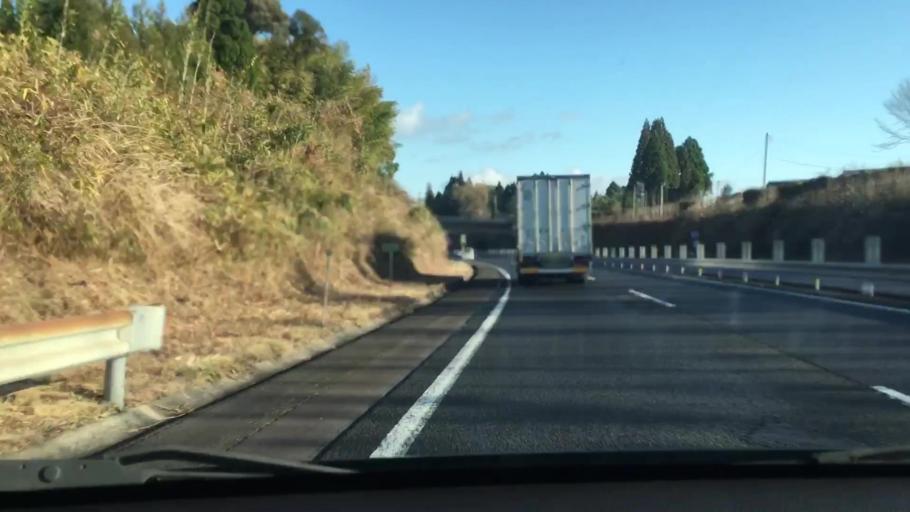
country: JP
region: Kagoshima
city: Kajiki
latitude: 31.8207
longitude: 130.6961
